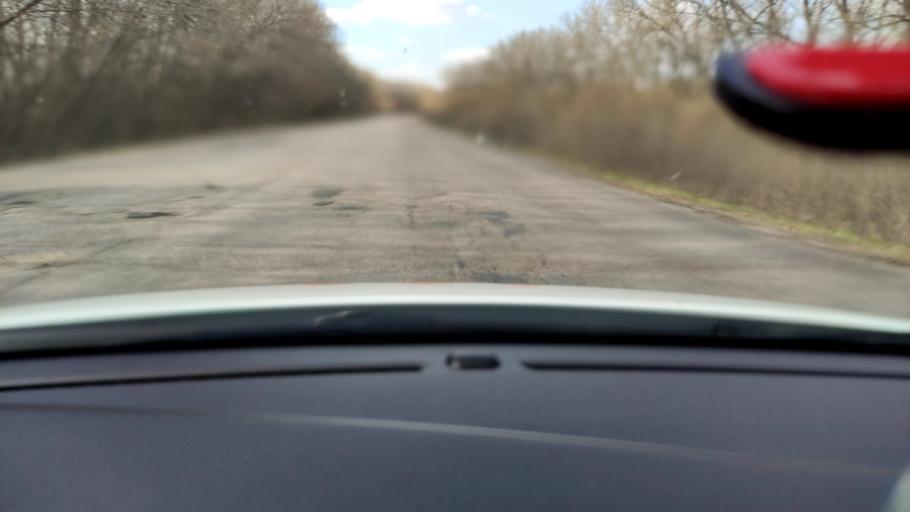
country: RU
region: Voronezj
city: Uryv-Pokrovka
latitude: 51.2240
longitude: 39.0630
